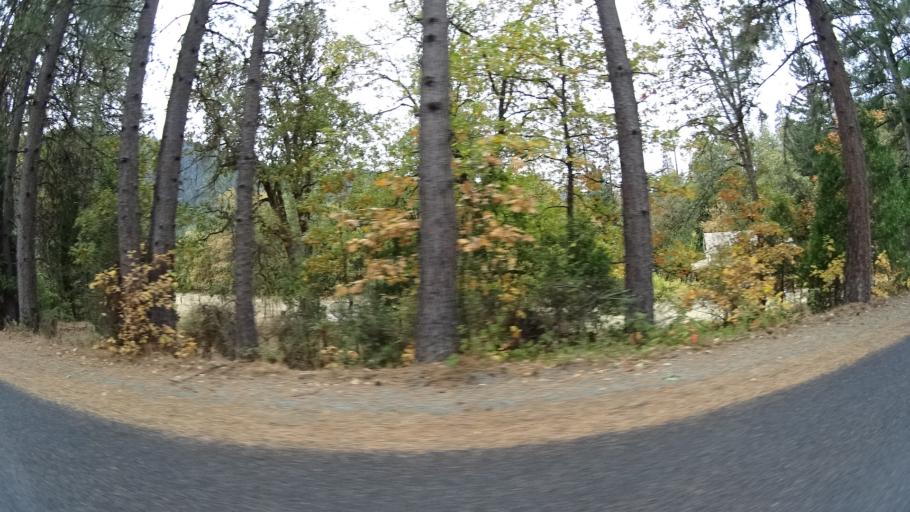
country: US
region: California
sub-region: Siskiyou County
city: Happy Camp
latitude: 41.8588
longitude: -123.1635
